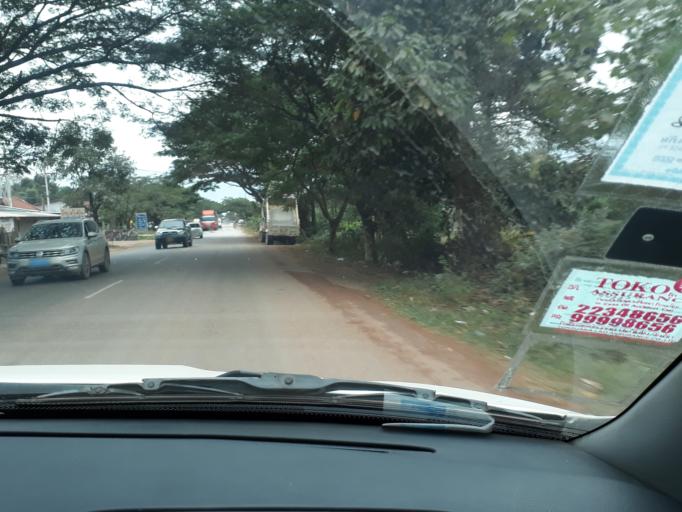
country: LA
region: Vientiane
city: Muang Phon-Hong
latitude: 18.3314
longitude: 102.4419
